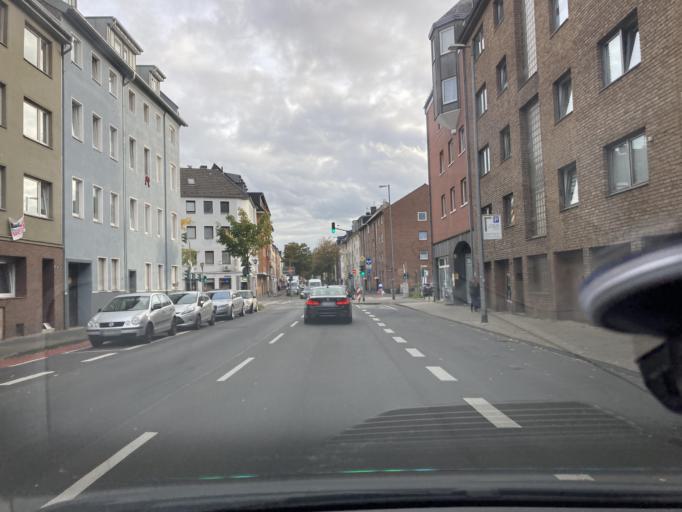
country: DE
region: North Rhine-Westphalia
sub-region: Regierungsbezirk Koln
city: Kalk
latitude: 50.9441
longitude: 7.0013
